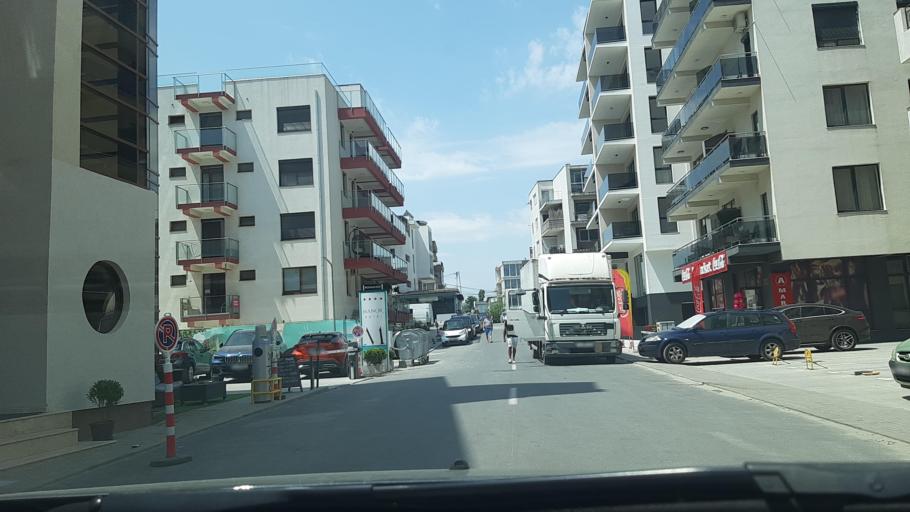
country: RO
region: Constanta
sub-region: Comuna Navodari
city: Navodari
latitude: 44.2982
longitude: 28.6245
